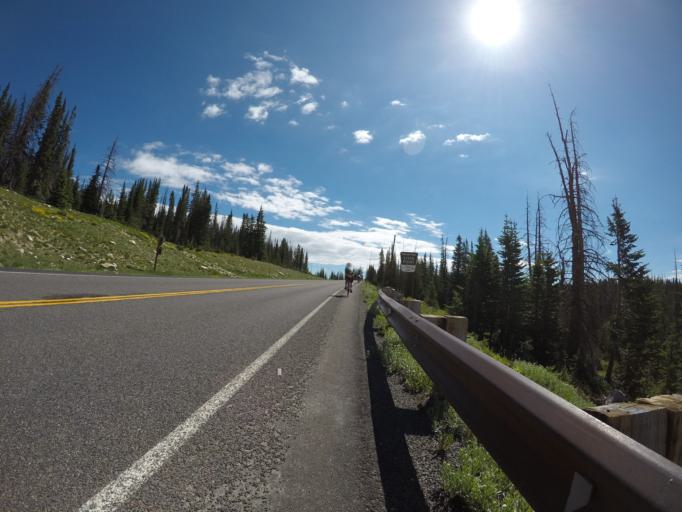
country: US
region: Wyoming
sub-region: Carbon County
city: Saratoga
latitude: 41.3137
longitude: -106.3530
